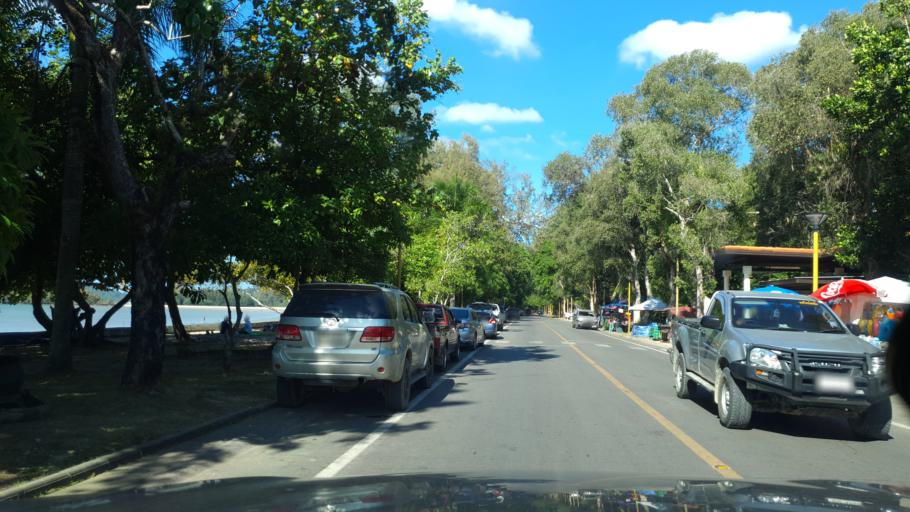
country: TH
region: Phangnga
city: Ban Ao Nang
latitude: 8.0449
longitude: 98.8058
